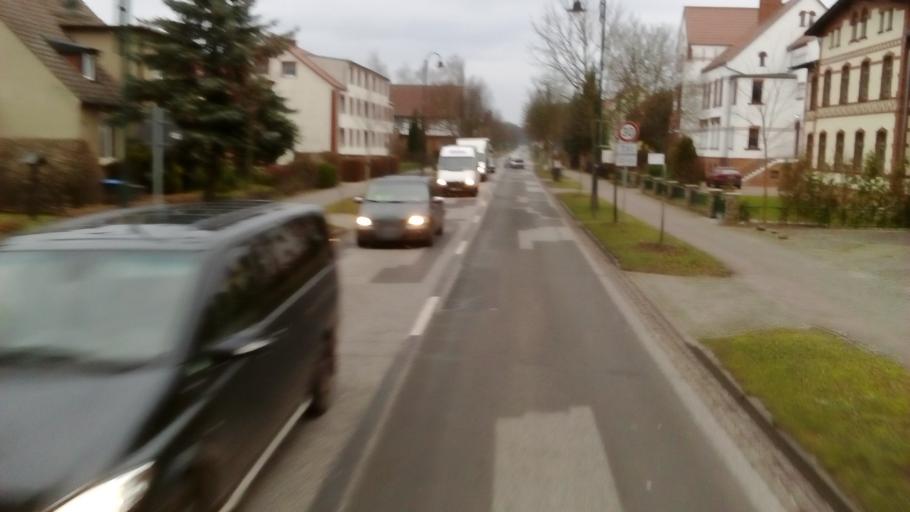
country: DE
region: Brandenburg
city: Brussow
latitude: 53.4530
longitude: 14.2181
